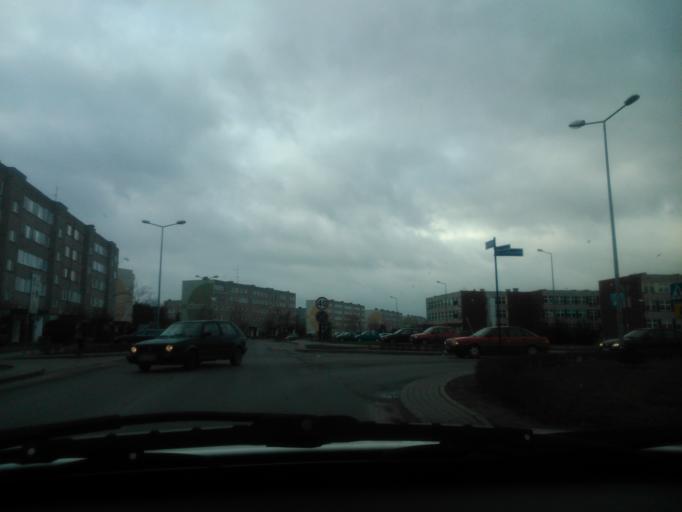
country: PL
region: Kujawsko-Pomorskie
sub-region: Powiat golubsko-dobrzynski
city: Golub-Dobrzyn
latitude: 53.1023
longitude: 19.0572
